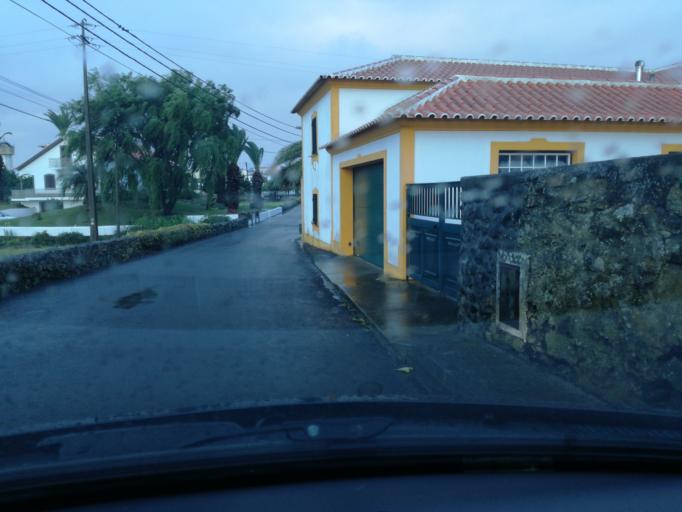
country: PT
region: Azores
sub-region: Praia da Vitoria
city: Praia da Vitoria
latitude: 38.7062
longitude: -27.0581
